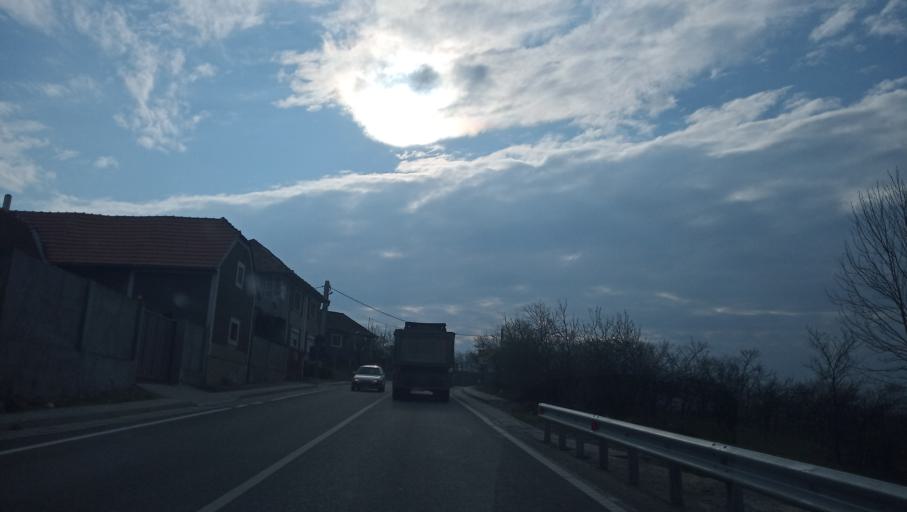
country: RO
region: Bihor
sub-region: Comuna Rieni
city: Rieni
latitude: 46.5818
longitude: 22.4392
